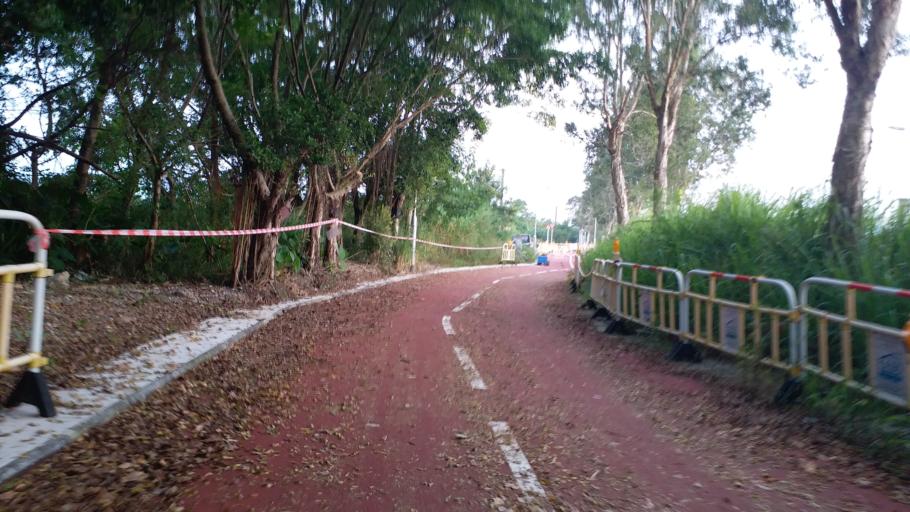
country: HK
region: Yuen Long
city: Yuen Long Kau Hui
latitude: 22.4623
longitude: 114.0459
